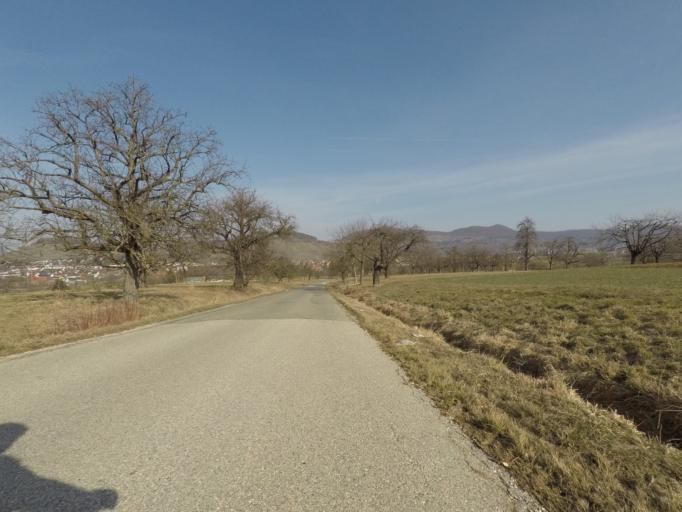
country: DE
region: Baden-Wuerttemberg
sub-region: Tuebingen Region
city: Metzingen
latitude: 48.5224
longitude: 9.3004
